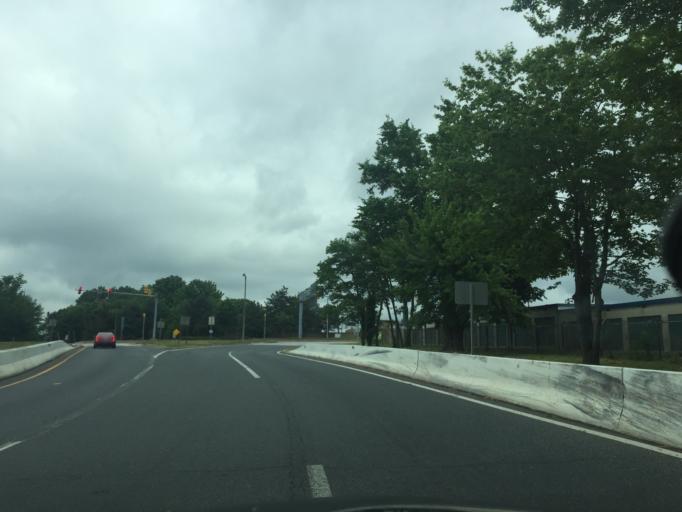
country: US
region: Maryland
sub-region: Baltimore County
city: Rosedale
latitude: 39.2872
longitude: -76.5318
